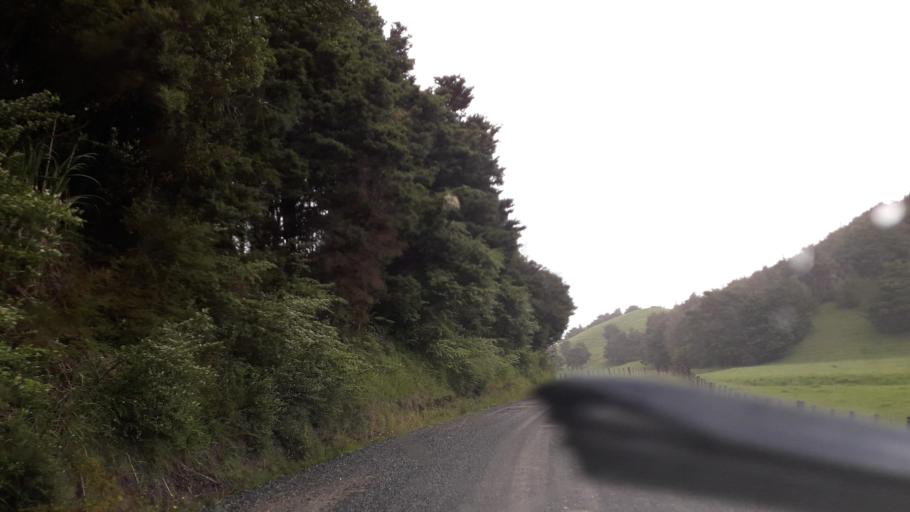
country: NZ
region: Northland
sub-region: Far North District
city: Kaitaia
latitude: -35.1086
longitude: 173.3953
